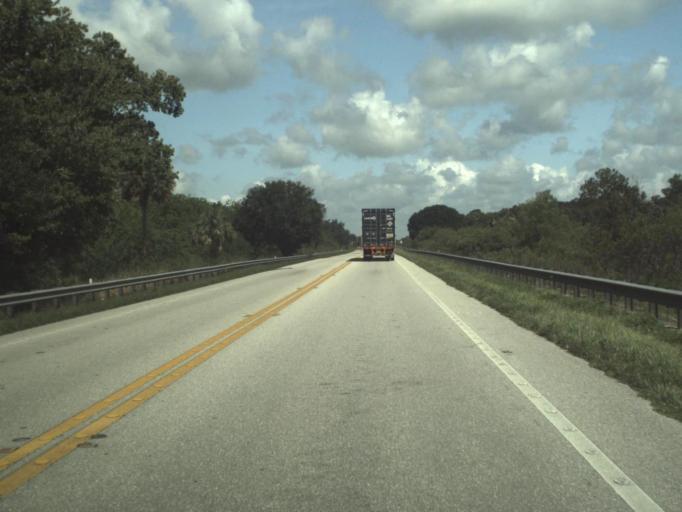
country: US
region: Florida
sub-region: Martin County
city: Indiantown
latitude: 27.0711
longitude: -80.5446
